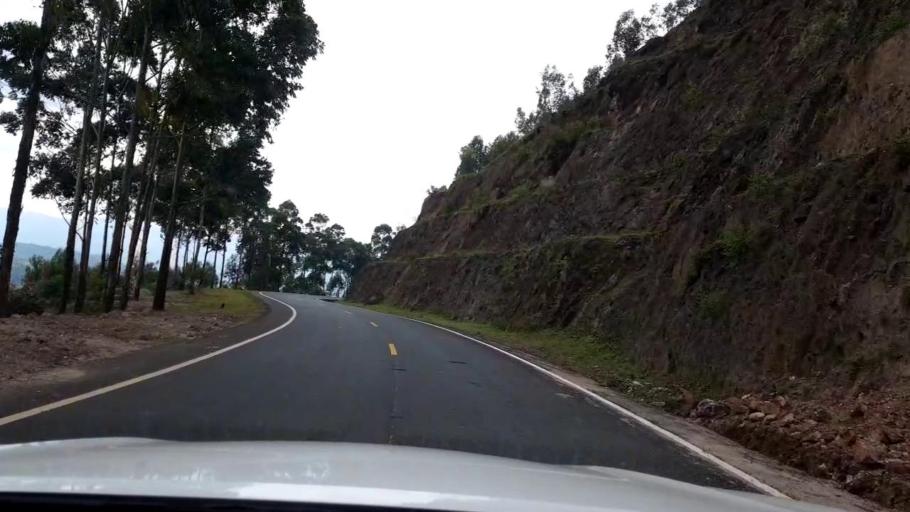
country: RW
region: Southern Province
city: Gitarama
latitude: -2.0244
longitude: 29.7163
